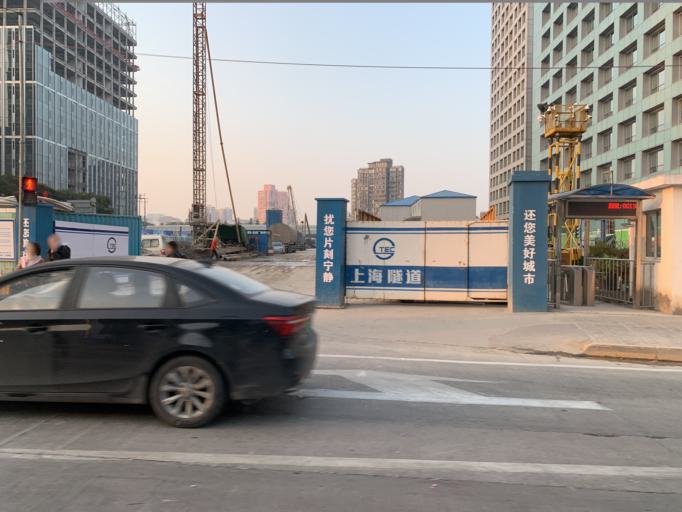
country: CN
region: Shanghai Shi
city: Huamu
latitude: 31.2276
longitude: 121.5453
